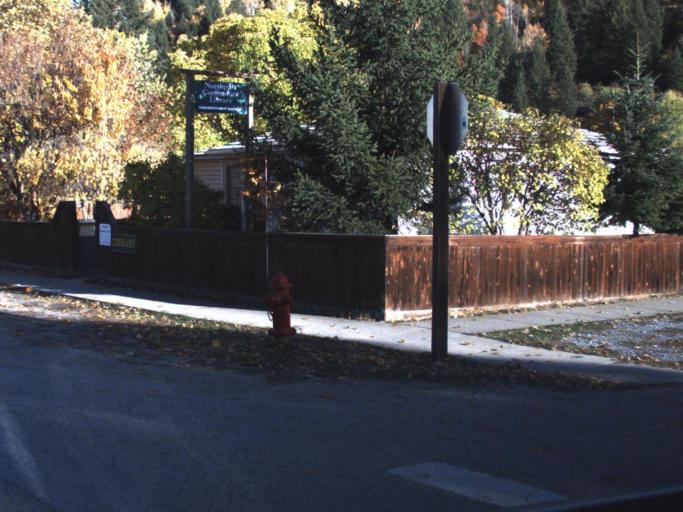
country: CA
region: British Columbia
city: Rossland
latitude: 48.9152
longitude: -117.7843
